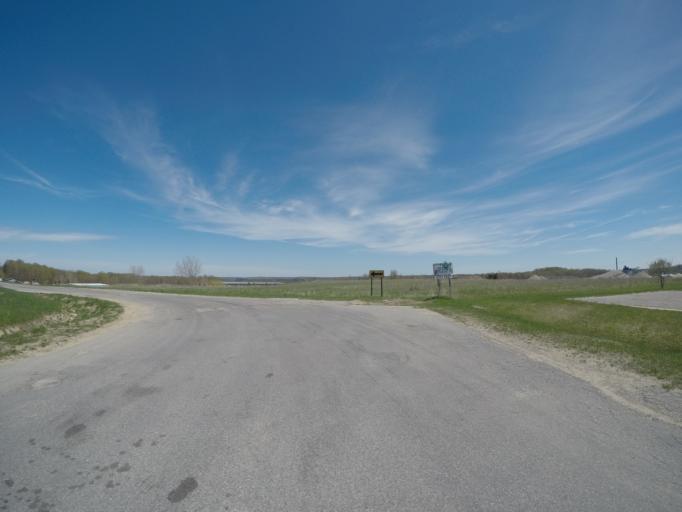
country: US
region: Michigan
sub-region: Grand Traverse County
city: Traverse City
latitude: 44.6943
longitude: -85.6524
